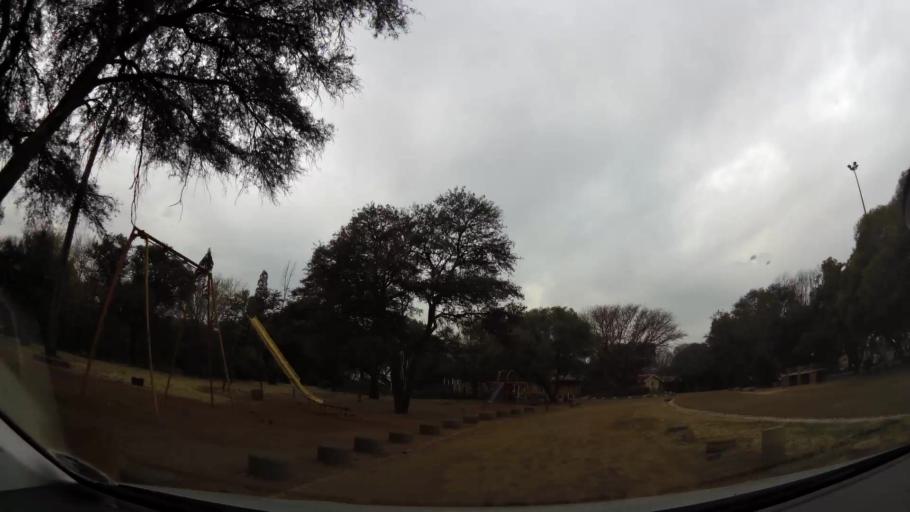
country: ZA
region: Gauteng
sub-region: City of Johannesburg Metropolitan Municipality
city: Soweto
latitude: -26.2438
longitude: 27.8690
